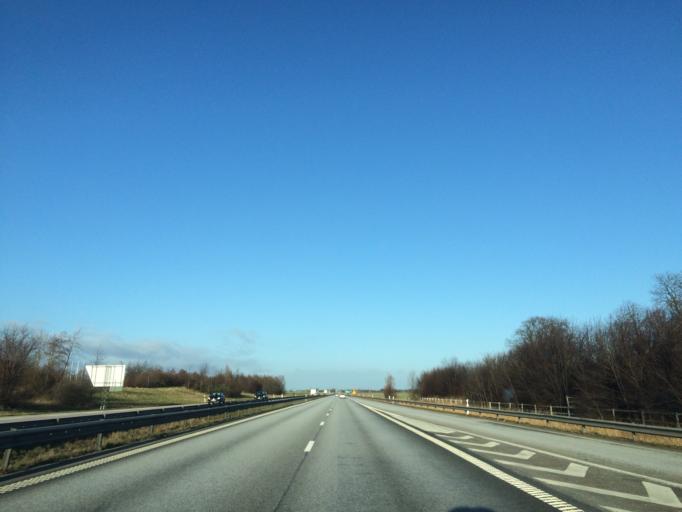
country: SE
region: Skane
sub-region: Lomma Kommun
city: Lomma
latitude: 55.6900
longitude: 13.0977
